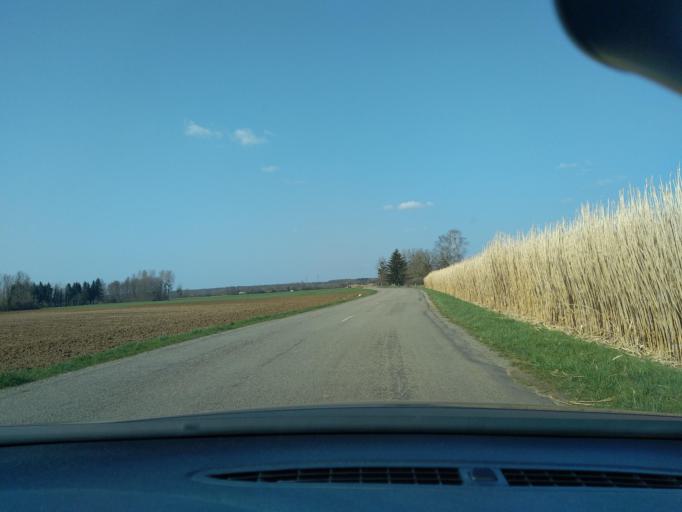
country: FR
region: Franche-Comte
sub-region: Departement du Jura
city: Mont-sous-Vaudrey
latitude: 46.9926
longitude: 5.6057
